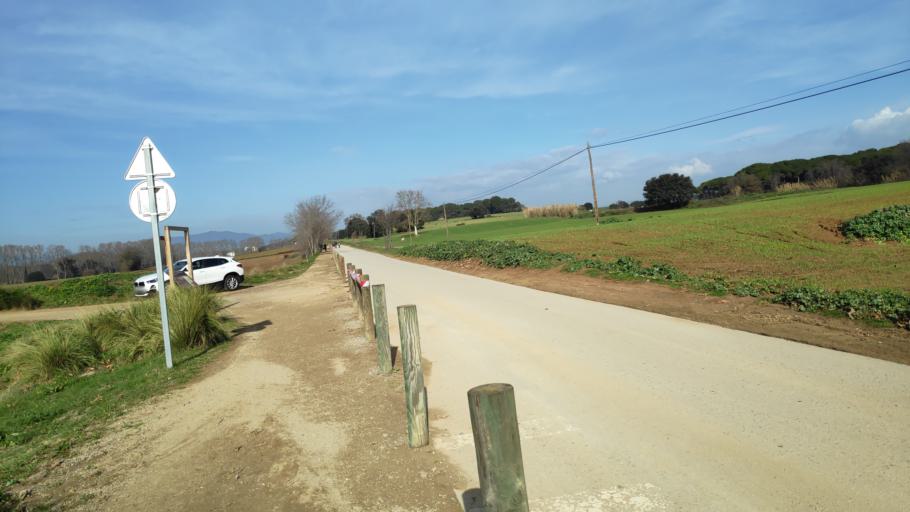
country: ES
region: Catalonia
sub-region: Provincia de Barcelona
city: Mollet del Valles
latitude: 41.5533
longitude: 2.2055
